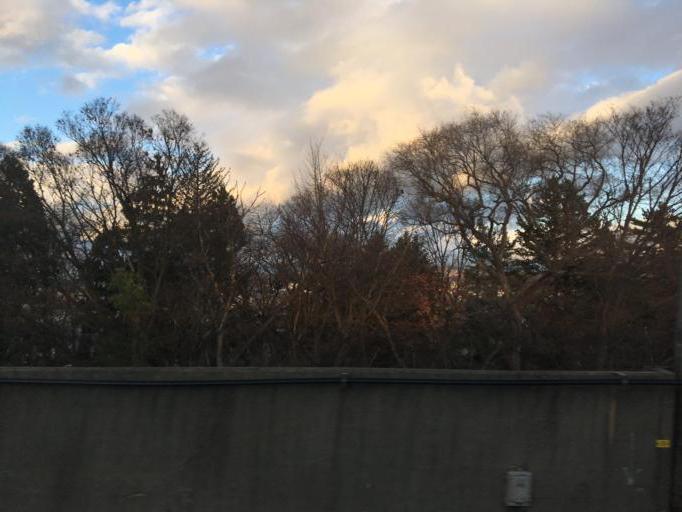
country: JP
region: Iwate
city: Morioka-shi
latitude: 39.7124
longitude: 141.1243
